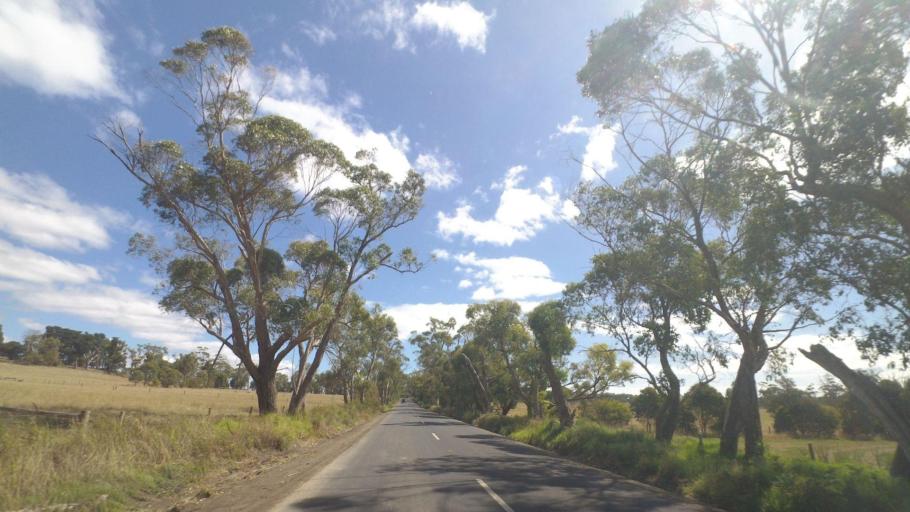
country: AU
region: Victoria
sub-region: Cardinia
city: Bunyip
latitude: -38.3337
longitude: 145.7028
